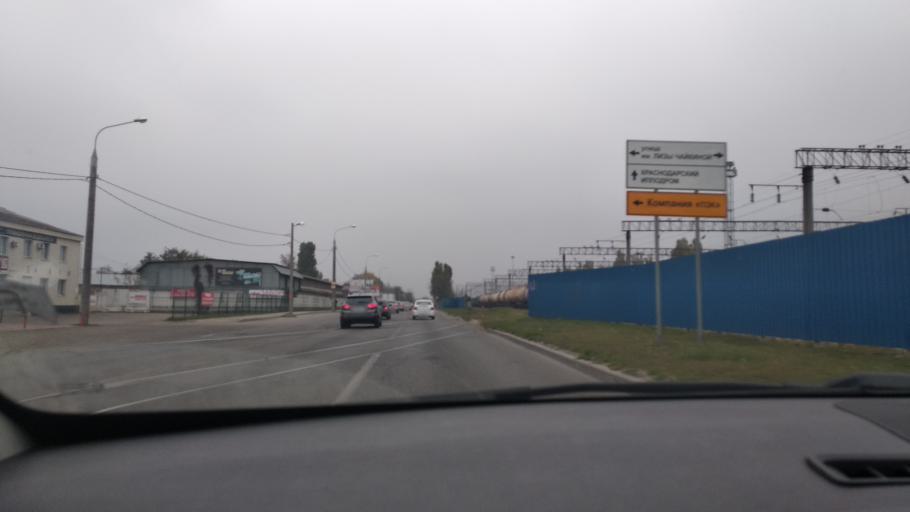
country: RU
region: Krasnodarskiy
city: Pashkovskiy
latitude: 45.0366
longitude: 39.0430
